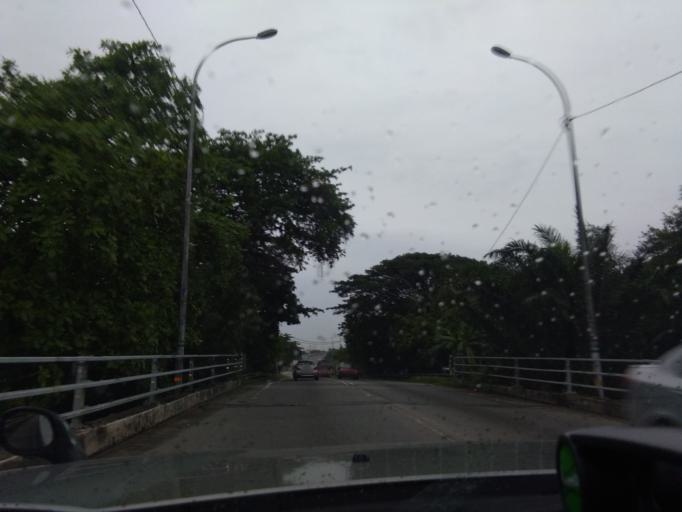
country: MY
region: Penang
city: Nibong Tebal
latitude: 5.1648
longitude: 100.4789
